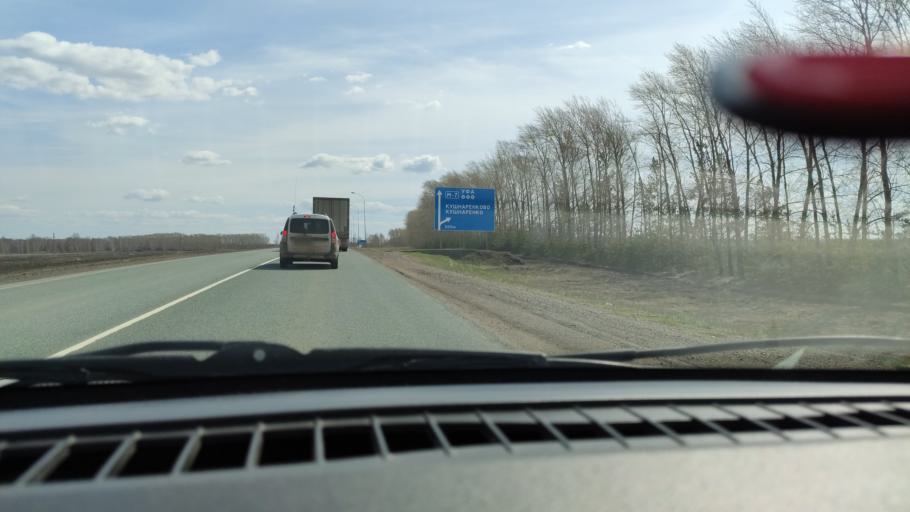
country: RU
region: Bashkortostan
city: Kushnarenkovo
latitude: 55.1396
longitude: 55.1658
